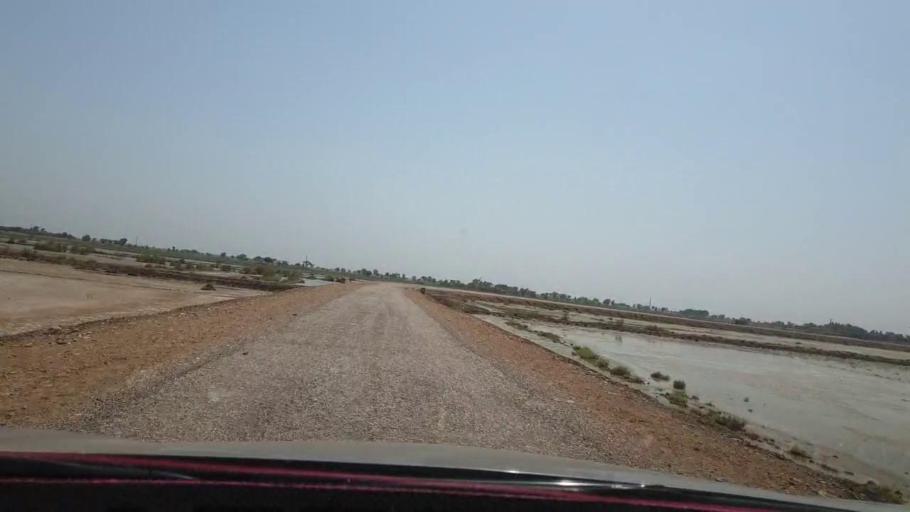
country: PK
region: Sindh
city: Warah
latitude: 27.5060
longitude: 67.7138
